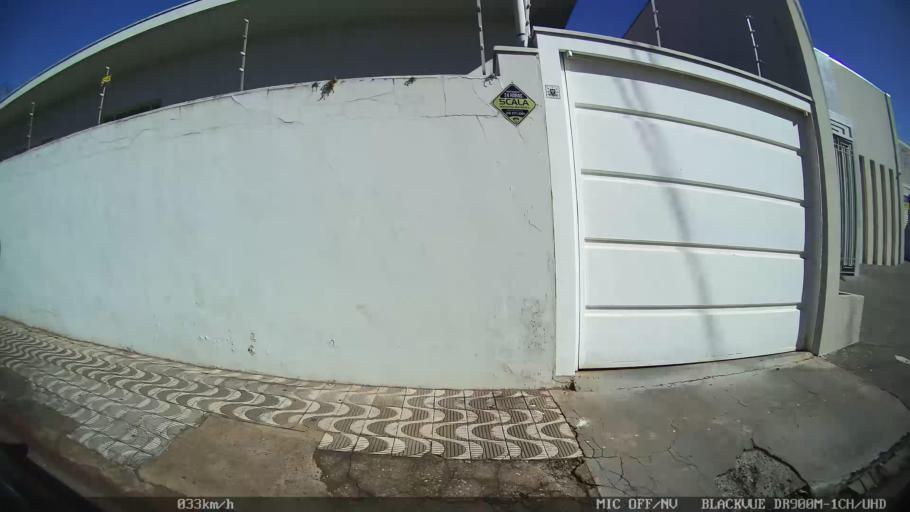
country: BR
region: Sao Paulo
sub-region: Franca
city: Franca
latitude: -20.5412
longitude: -47.3999
